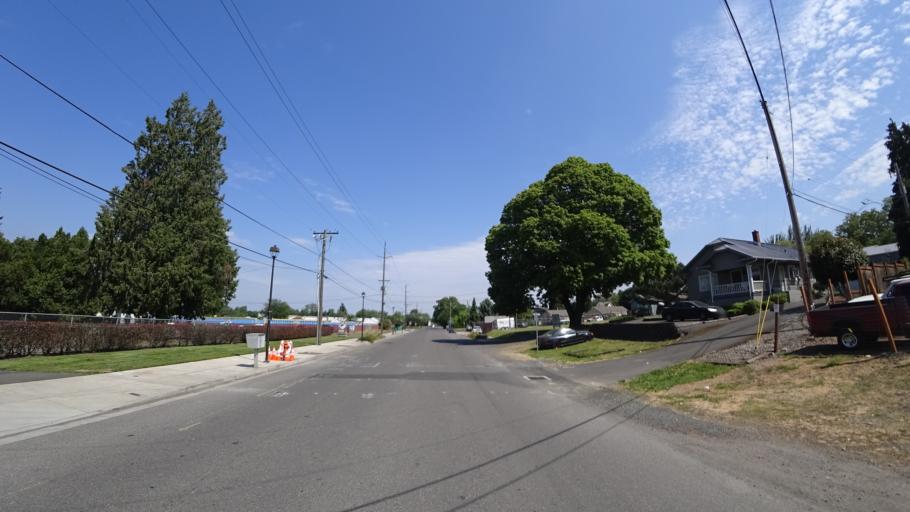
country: US
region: Oregon
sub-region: Multnomah County
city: Lents
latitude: 45.5607
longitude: -122.5496
